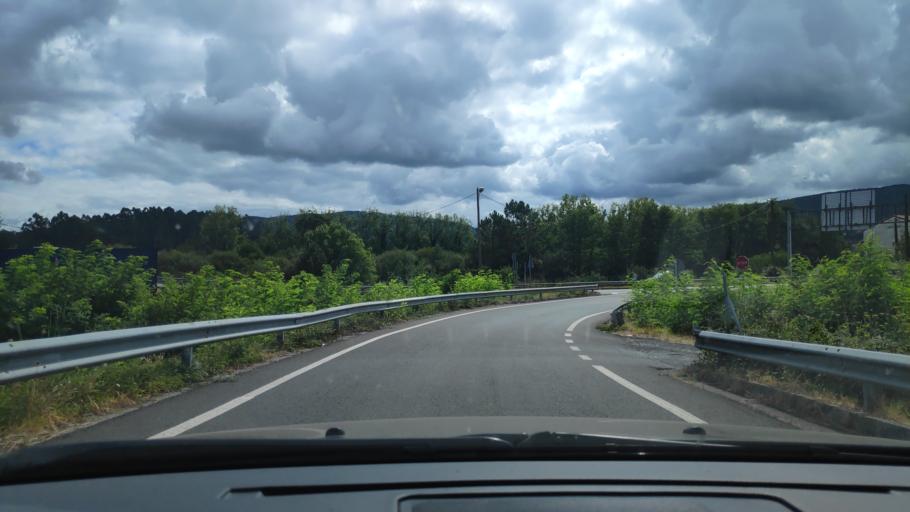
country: ES
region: Galicia
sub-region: Provincia da Coruna
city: Padron
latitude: 42.7308
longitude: -8.6585
